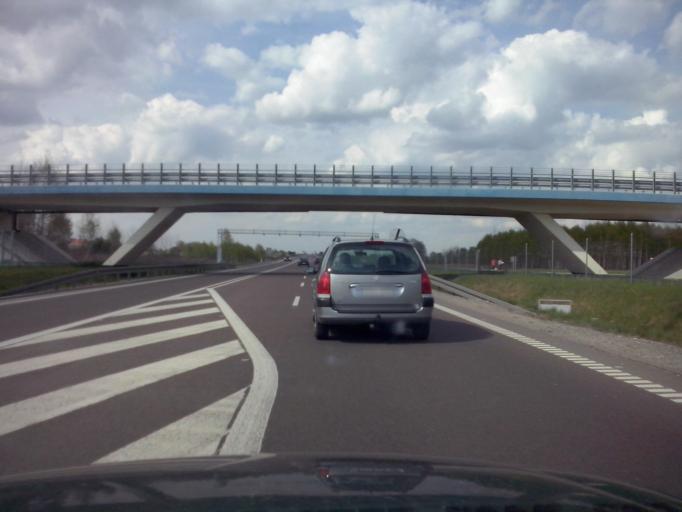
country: PL
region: Subcarpathian Voivodeship
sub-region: Powiat rzeszowski
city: Wolka Podlesna
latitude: 50.1286
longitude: 22.0808
